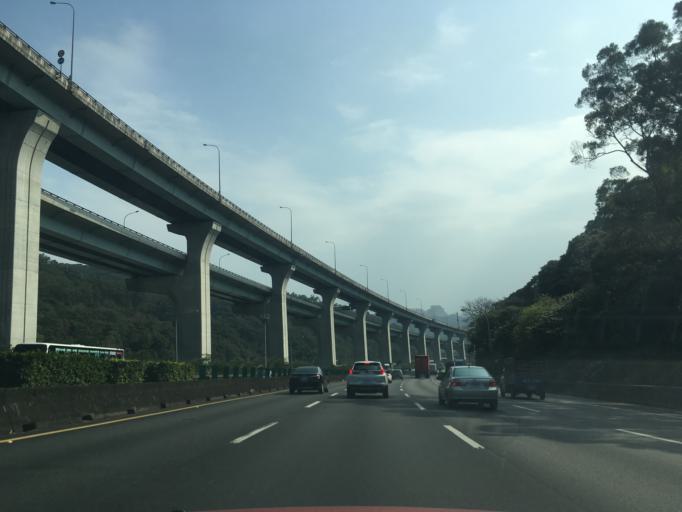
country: TW
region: Taipei
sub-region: Taipei
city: Banqiao
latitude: 25.0640
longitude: 121.3918
